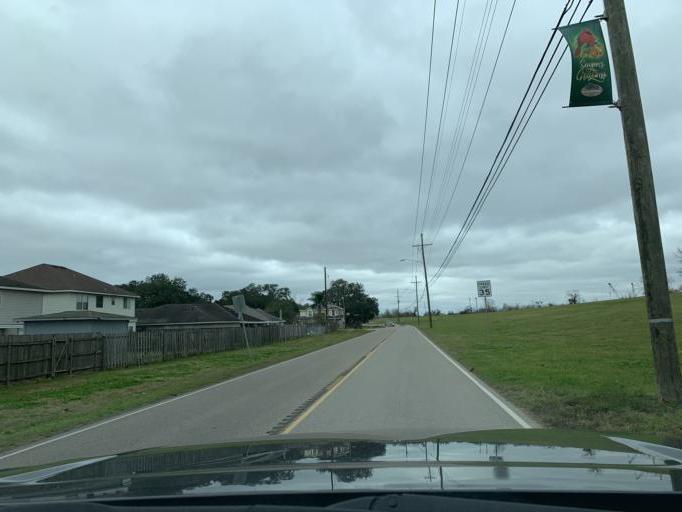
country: US
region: Louisiana
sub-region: Jefferson Parish
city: River Ridge
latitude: 29.9515
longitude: -90.2329
